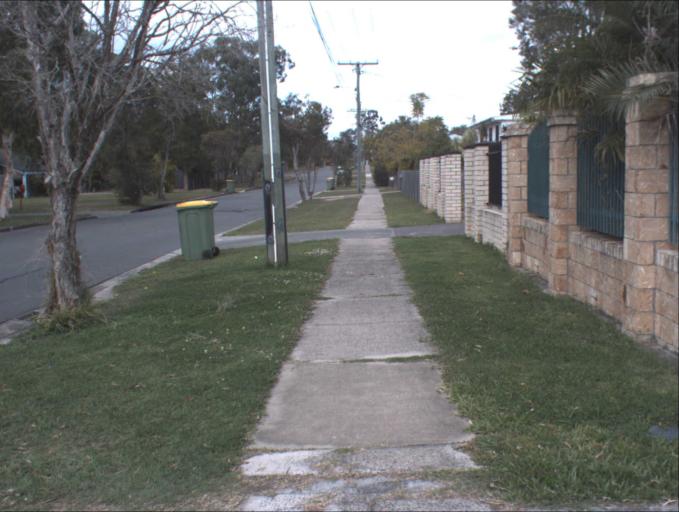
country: AU
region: Queensland
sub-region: Logan
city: Waterford West
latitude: -27.6739
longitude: 153.1288
